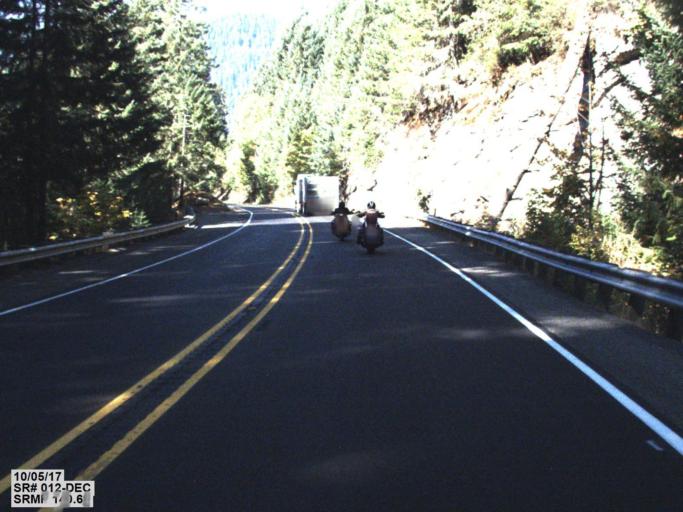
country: US
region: Washington
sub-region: Pierce County
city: Buckley
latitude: 46.6888
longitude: -121.5531
